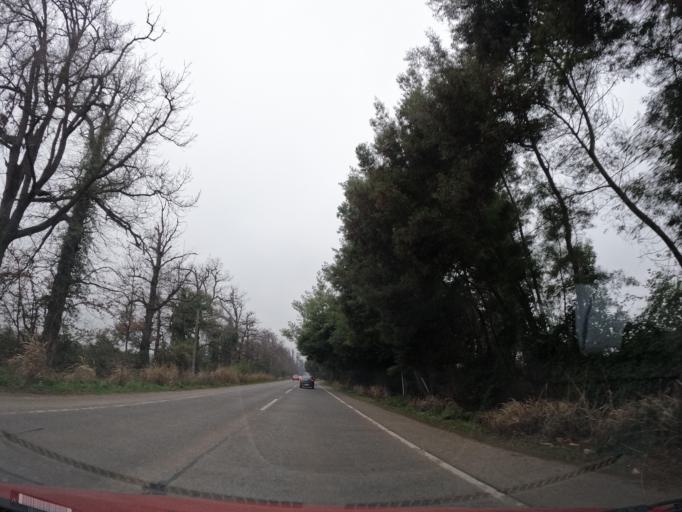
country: CL
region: Maule
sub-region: Provincia de Talca
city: San Clemente
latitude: -35.5626
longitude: -71.4552
